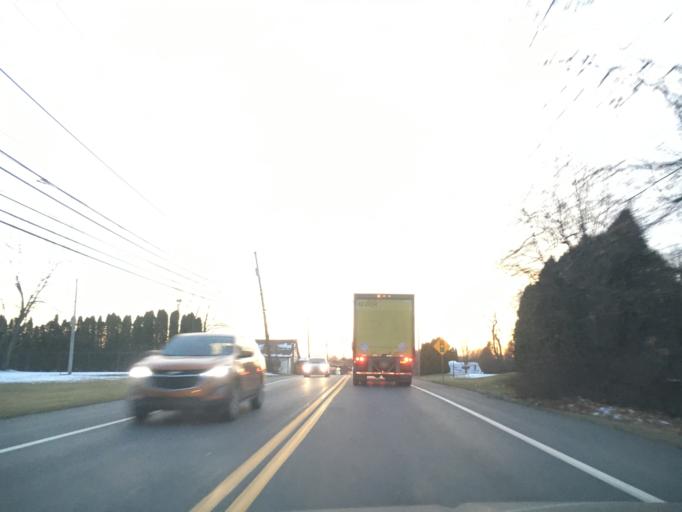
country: US
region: Pennsylvania
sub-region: Northampton County
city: Wind Gap
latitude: 40.8058
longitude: -75.3415
